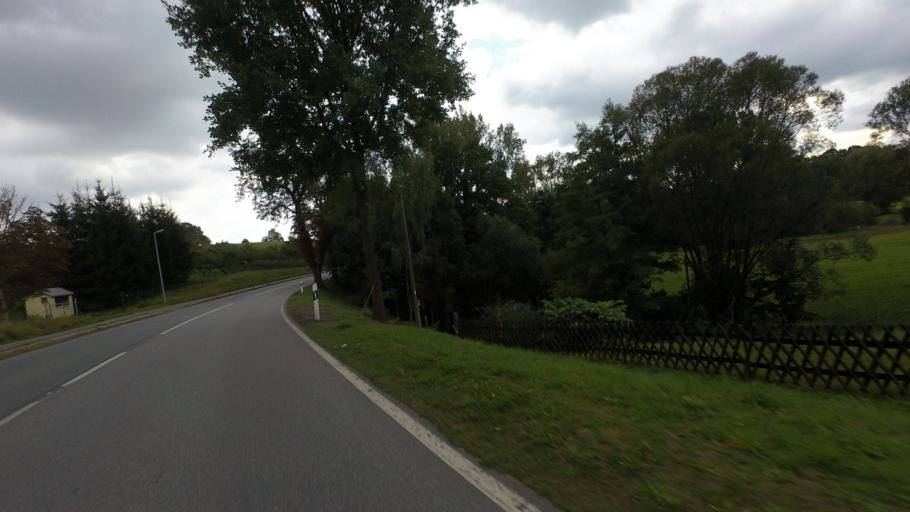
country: DE
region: Saxony
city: Grosspostwitz
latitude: 51.1107
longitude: 14.4562
